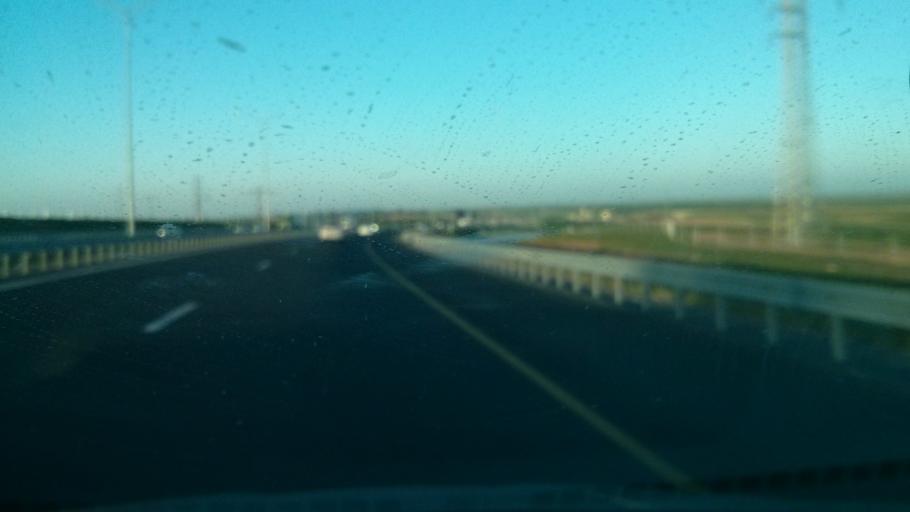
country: IL
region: Southern District
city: Lehavim
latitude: 31.4604
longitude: 34.7699
